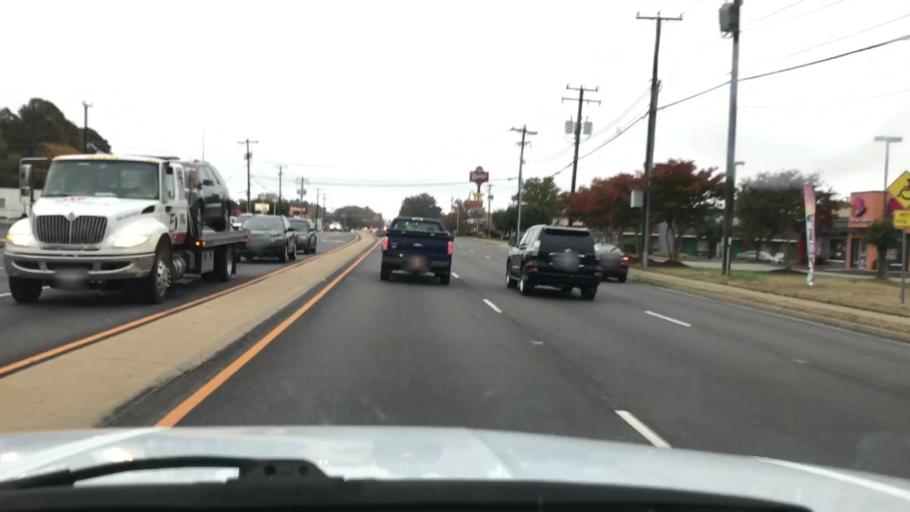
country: US
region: Virginia
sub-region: Henrico County
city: Chamberlayne
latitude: 37.6379
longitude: -77.4596
